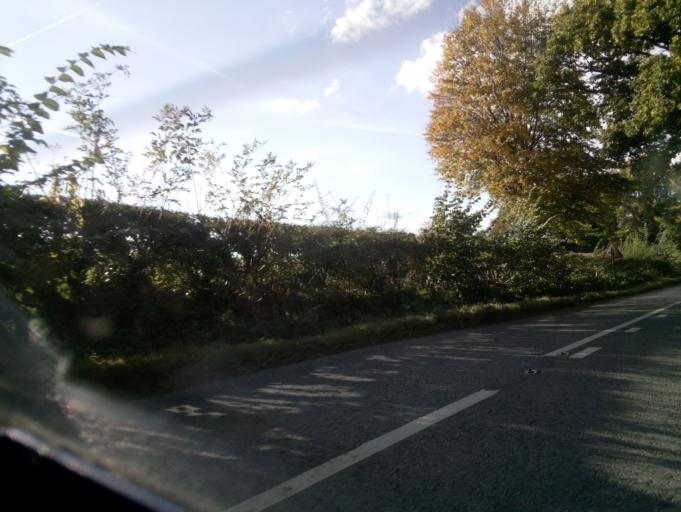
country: GB
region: England
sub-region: Herefordshire
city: Kinnersley
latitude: 52.1091
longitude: -2.9629
